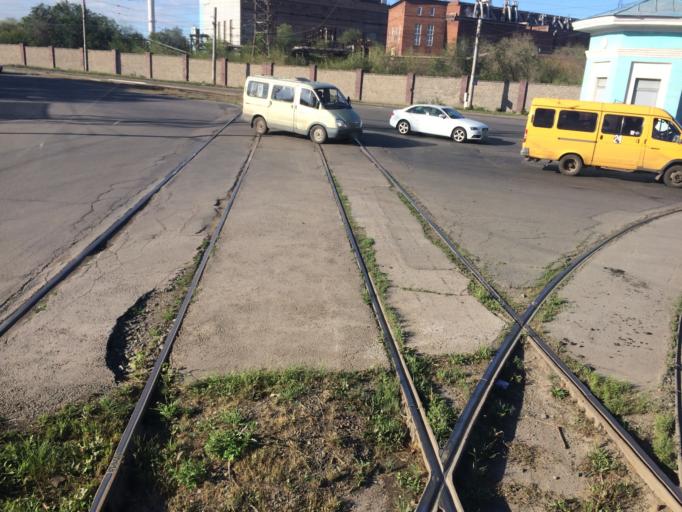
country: RU
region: Chelyabinsk
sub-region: Gorod Magnitogorsk
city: Magnitogorsk
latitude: 53.3981
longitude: 59.0232
